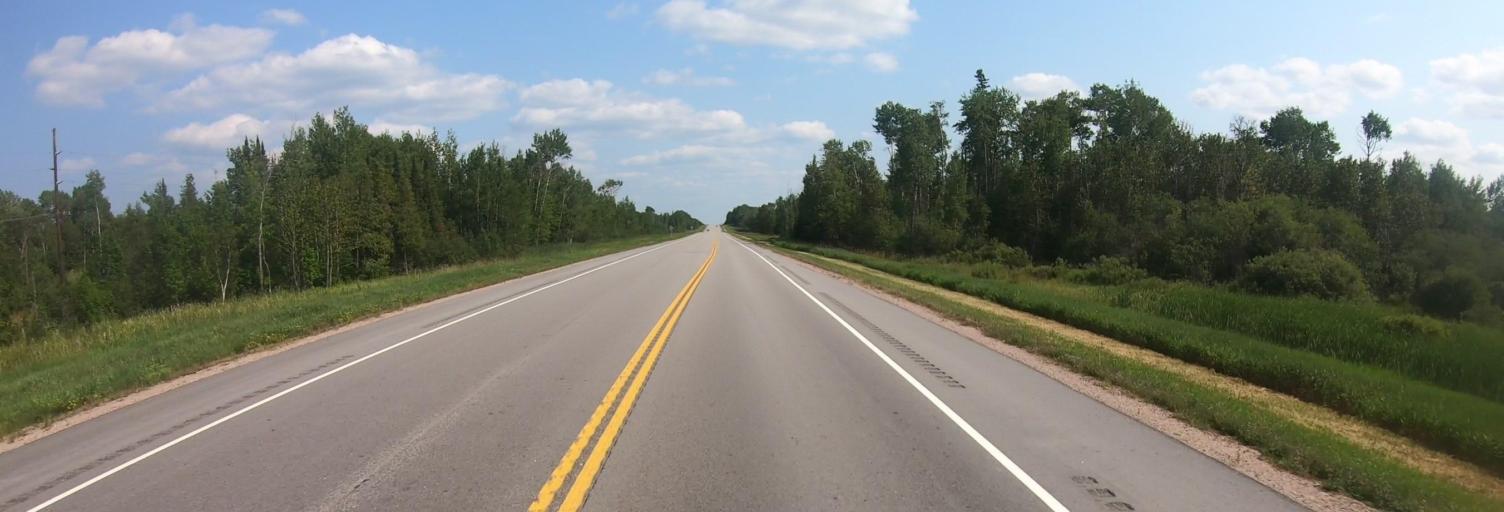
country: US
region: Minnesota
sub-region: Saint Louis County
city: Mountain Iron
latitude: 47.9225
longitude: -92.8202
